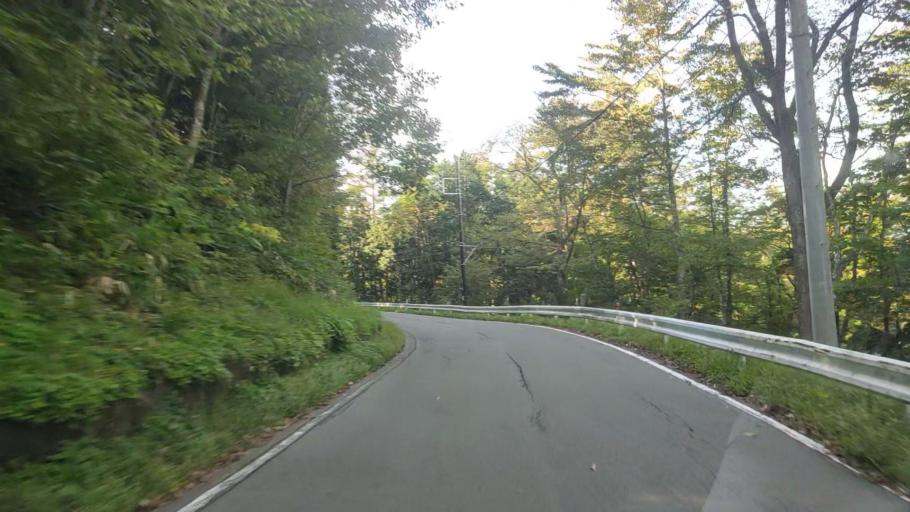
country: JP
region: Gunma
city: Nakanojomachi
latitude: 36.6061
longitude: 138.6842
